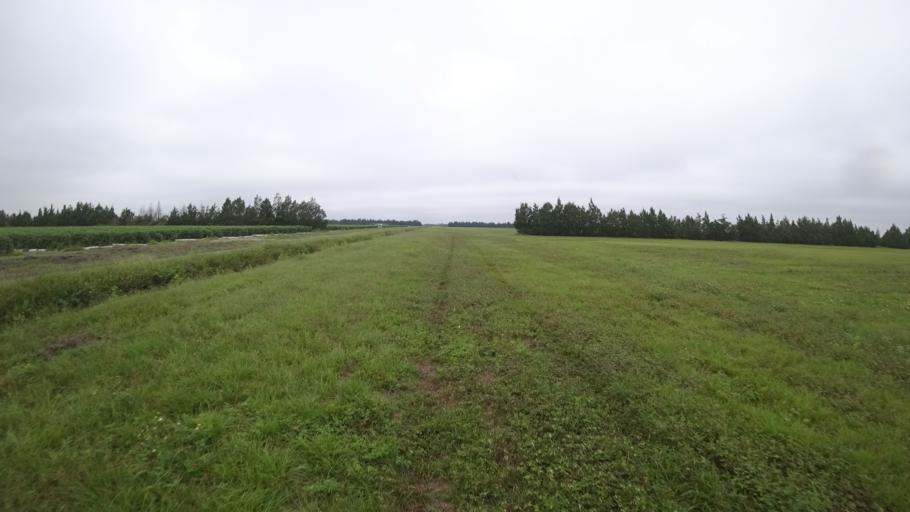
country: US
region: Florida
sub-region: Sarasota County
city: Warm Mineral Springs
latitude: 27.3024
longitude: -82.1490
